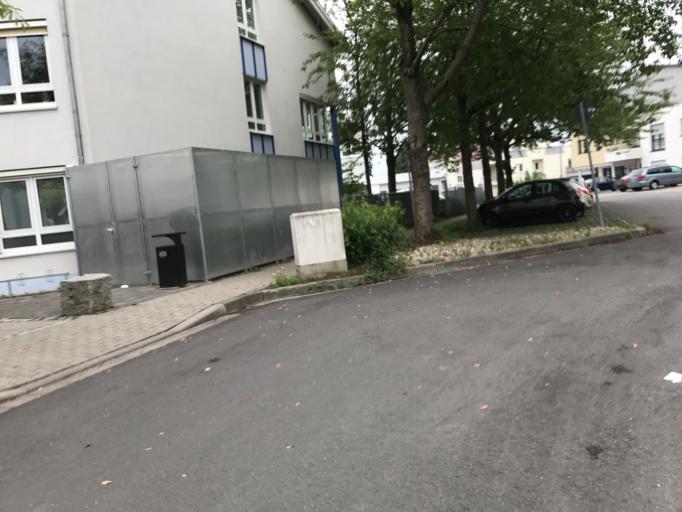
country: DE
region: Rheinland-Pfalz
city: Klein-Winternheim
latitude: 49.9692
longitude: 8.2390
